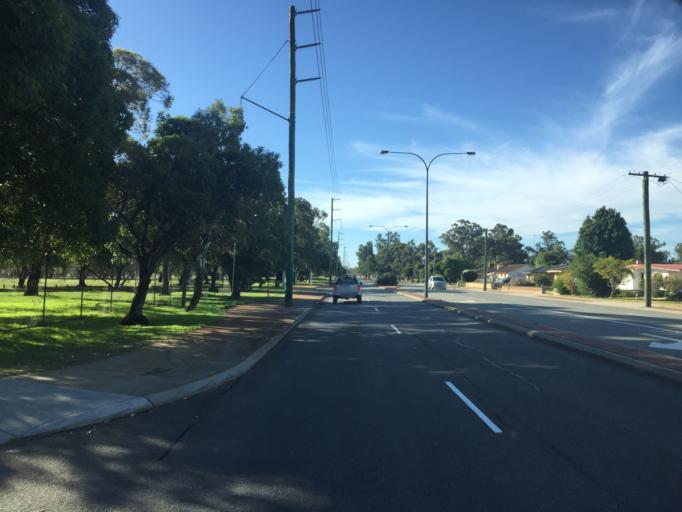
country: AU
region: Western Australia
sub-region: Belmont
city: Kewdale
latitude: -31.9717
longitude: 115.9470
